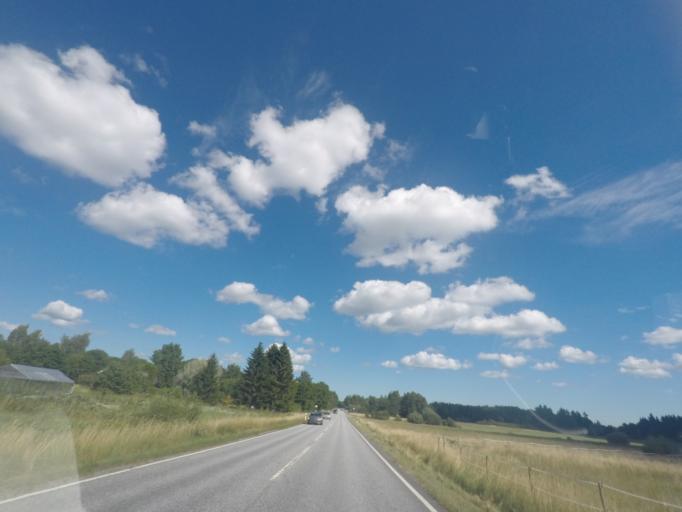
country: SE
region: Stockholm
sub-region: Norrtalje Kommun
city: Hallstavik
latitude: 59.9455
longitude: 18.7555
